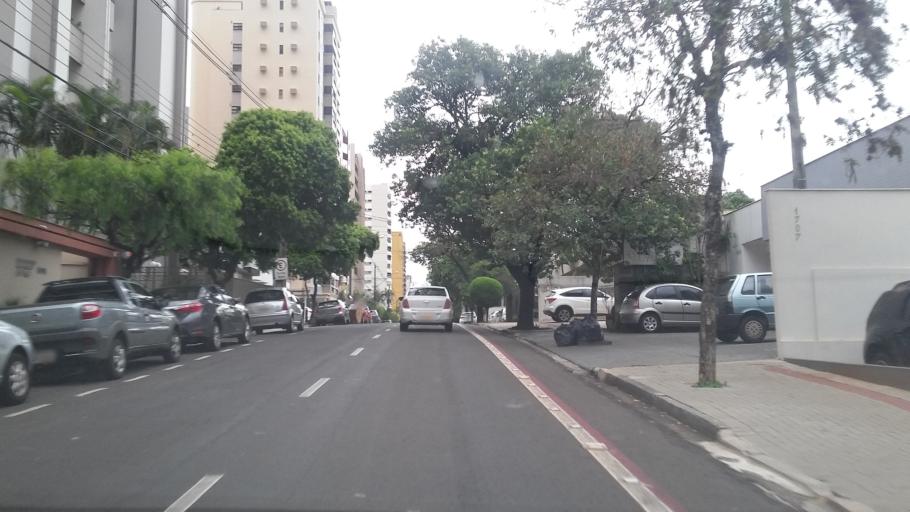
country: BR
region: Parana
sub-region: Londrina
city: Londrina
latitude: -23.3177
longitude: -51.1689
